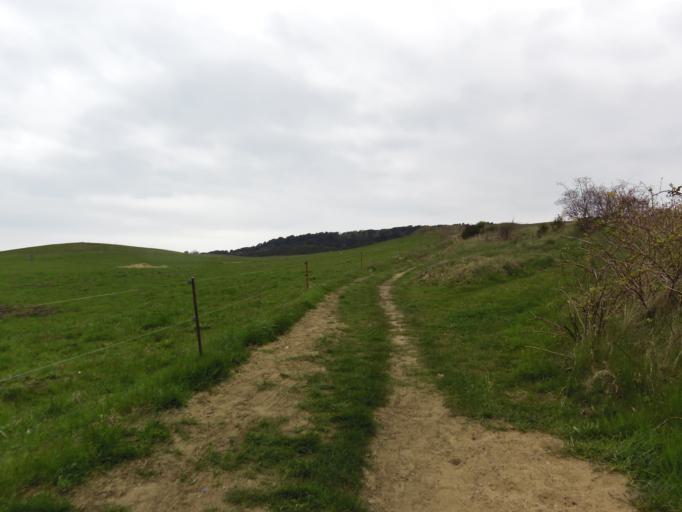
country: DE
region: Mecklenburg-Vorpommern
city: Hiddensee
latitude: 54.5919
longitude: 13.1264
